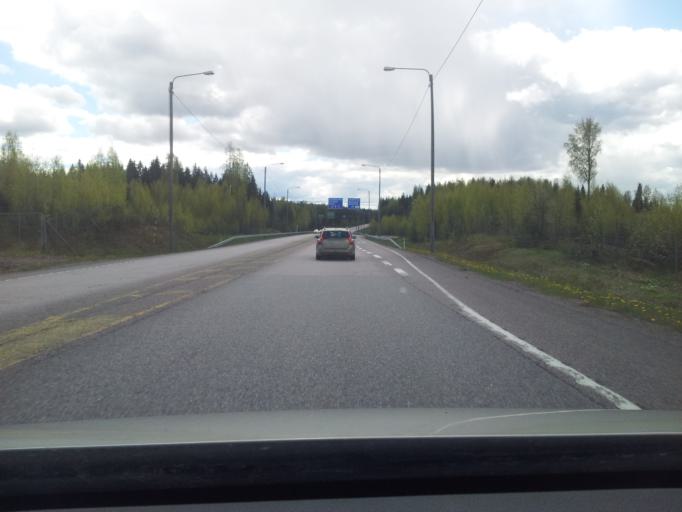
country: FI
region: Uusimaa
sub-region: Loviisa
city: Perna
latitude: 60.5162
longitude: 25.9634
